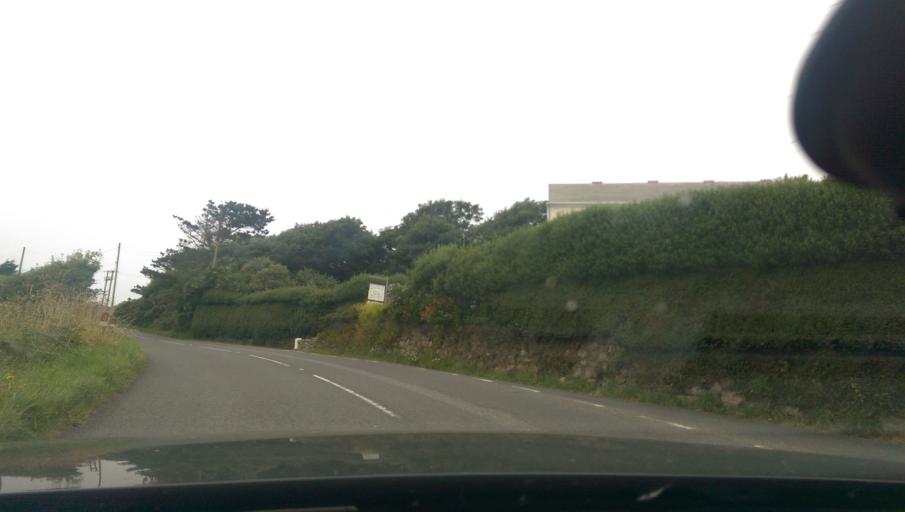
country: GB
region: England
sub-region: Cornwall
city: Saint Just
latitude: 50.1136
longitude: -5.6774
